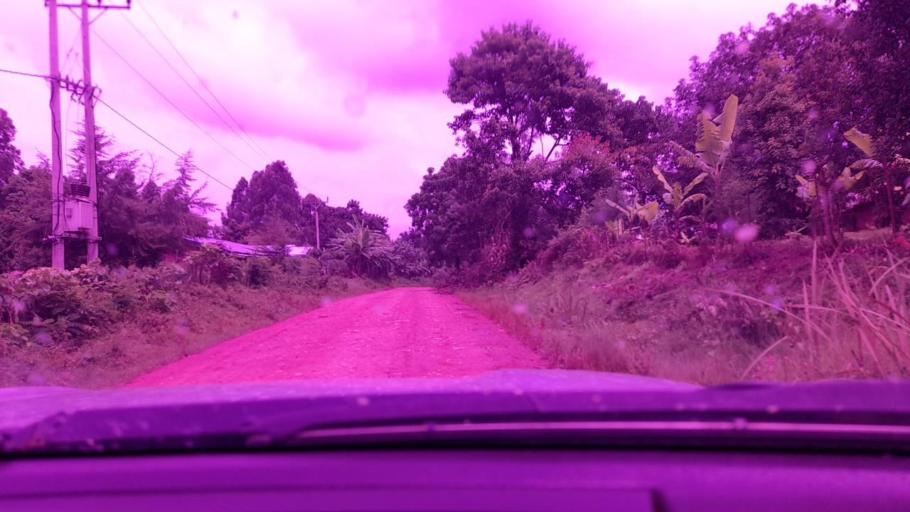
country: ET
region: Southern Nations, Nationalities, and People's Region
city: Bonga
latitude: 7.5449
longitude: 35.8767
